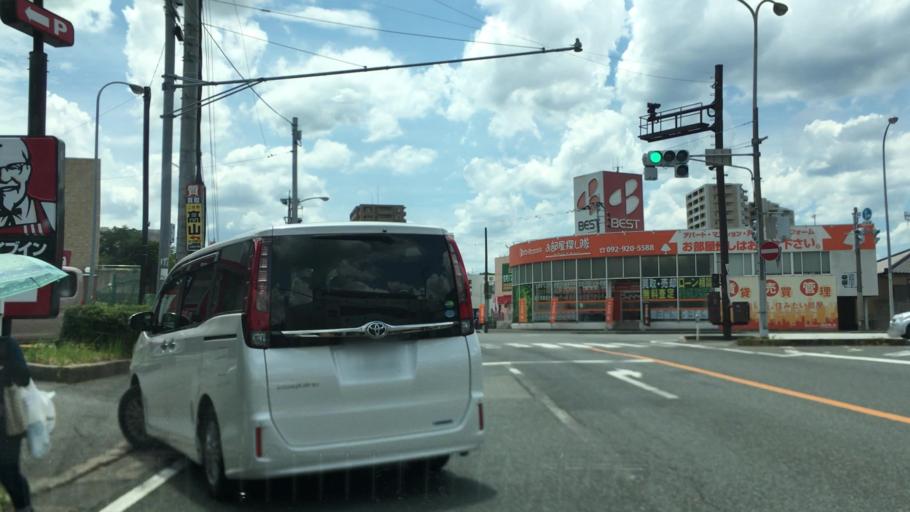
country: JP
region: Fukuoka
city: Dazaifu
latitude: 33.5087
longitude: 130.5240
